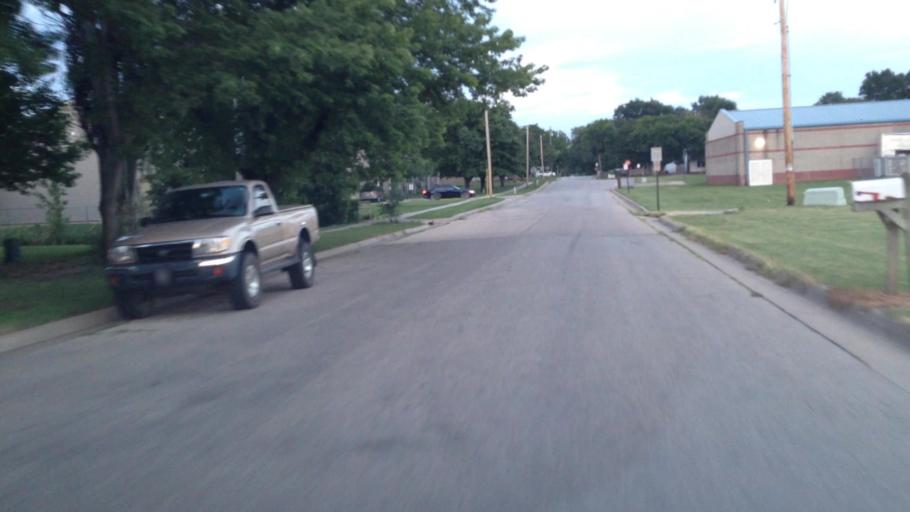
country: US
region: Kansas
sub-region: Montgomery County
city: Independence
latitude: 37.2400
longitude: -95.7128
